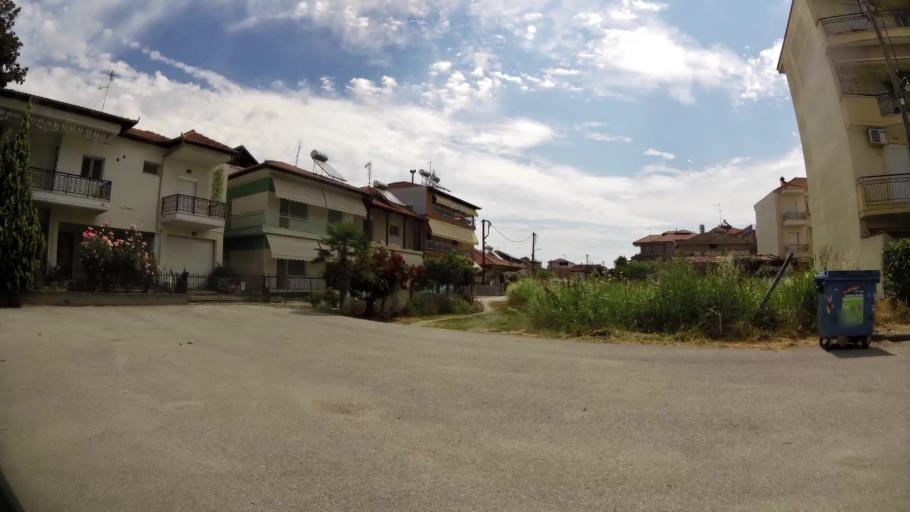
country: GR
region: Central Macedonia
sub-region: Nomos Pierias
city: Katerini
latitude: 40.2766
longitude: 22.4958
